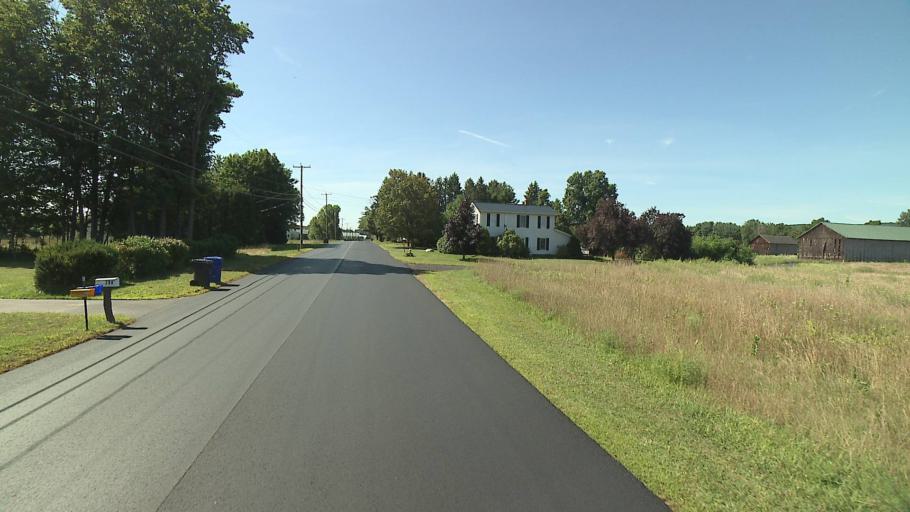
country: US
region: Connecticut
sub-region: Hartford County
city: Suffield Depot
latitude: 41.9859
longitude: -72.7054
